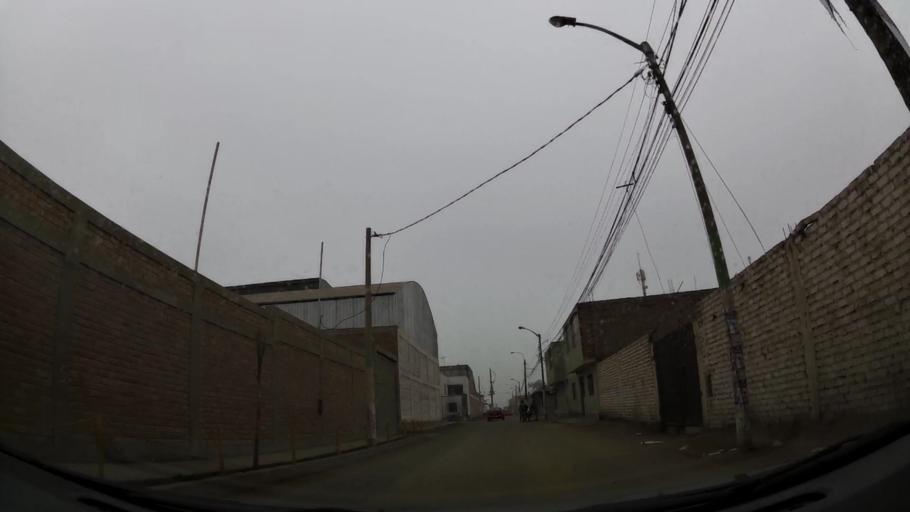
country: PE
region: Lima
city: Ventanilla
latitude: -11.8412
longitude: -77.1018
